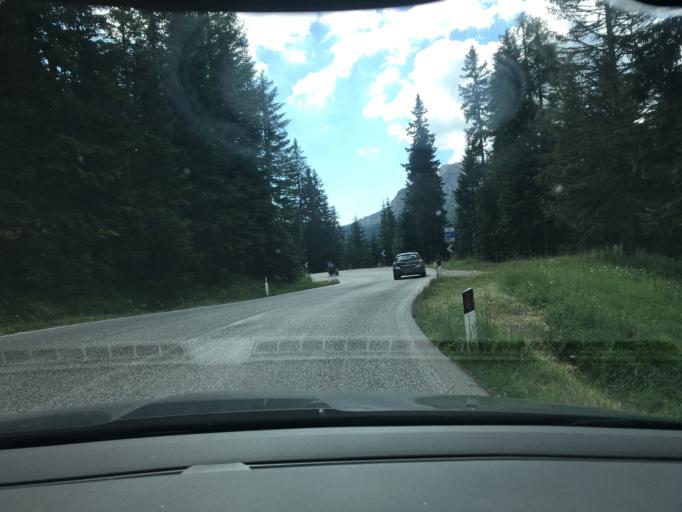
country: IT
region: Veneto
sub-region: Provincia di Belluno
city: Cortina d'Ampezzo
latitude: 46.5211
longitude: 12.0749
